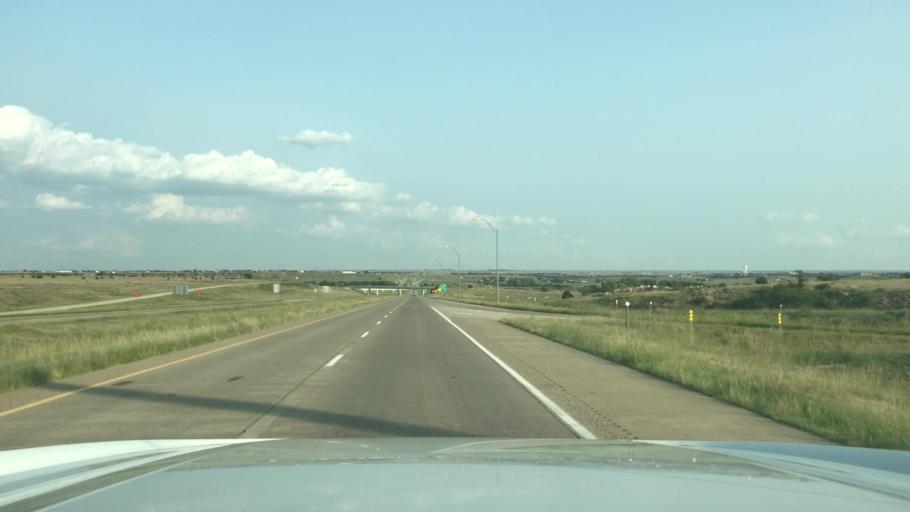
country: US
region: Texas
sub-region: Randall County
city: Canyon
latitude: 35.0197
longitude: -101.9166
